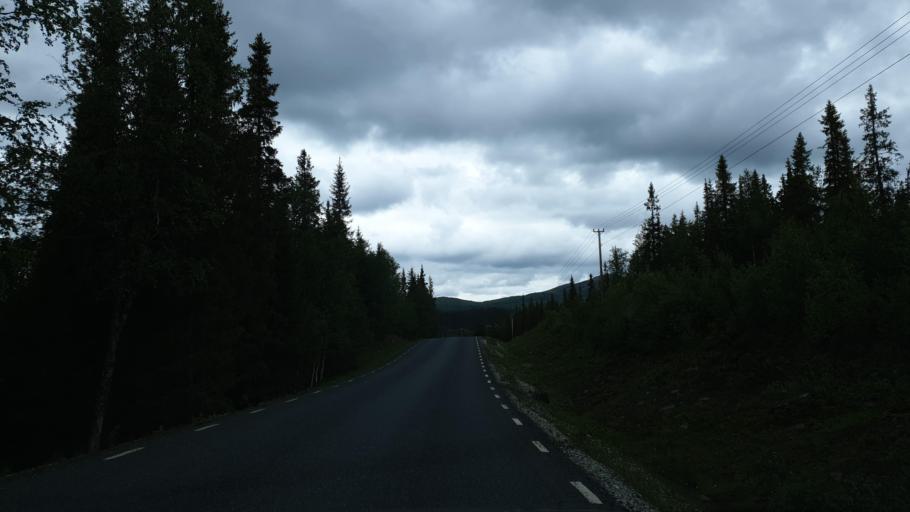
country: SE
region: Vaesterbotten
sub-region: Vilhelmina Kommun
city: Sjoberg
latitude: 65.2648
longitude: 15.3760
